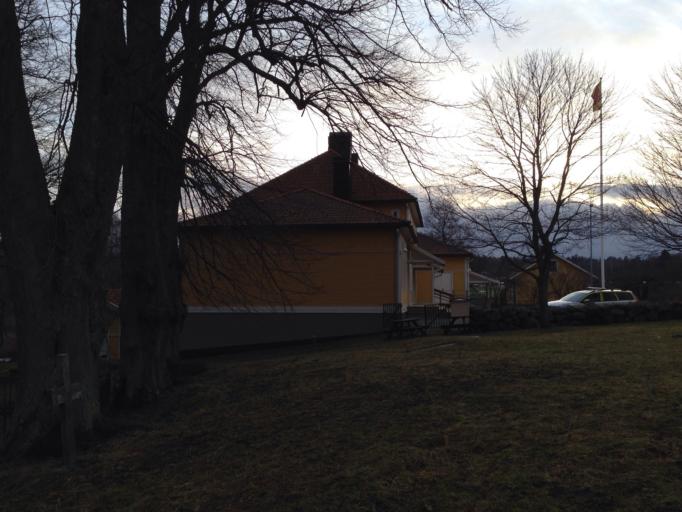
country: SE
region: Stockholm
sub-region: Salems Kommun
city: Ronninge
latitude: 59.2183
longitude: 17.7707
